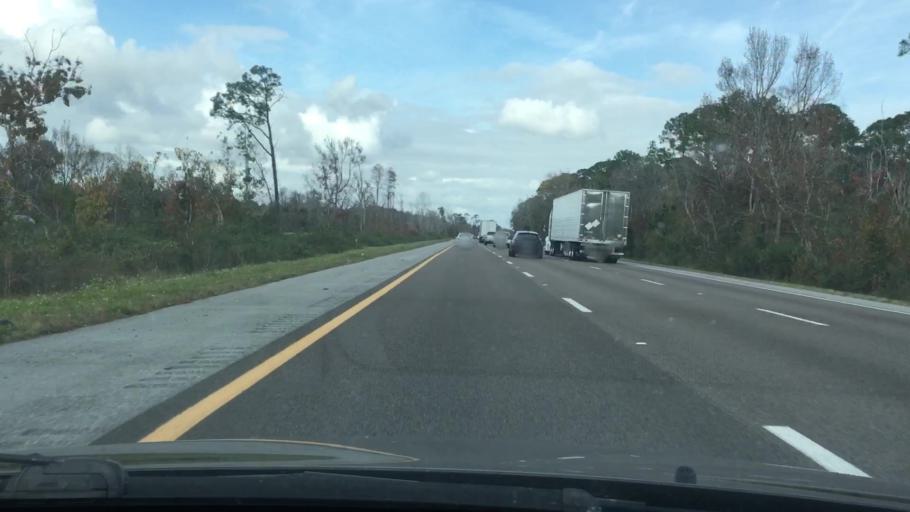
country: US
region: Florida
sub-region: Volusia County
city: Oak Hill
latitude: 28.8987
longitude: -80.9303
